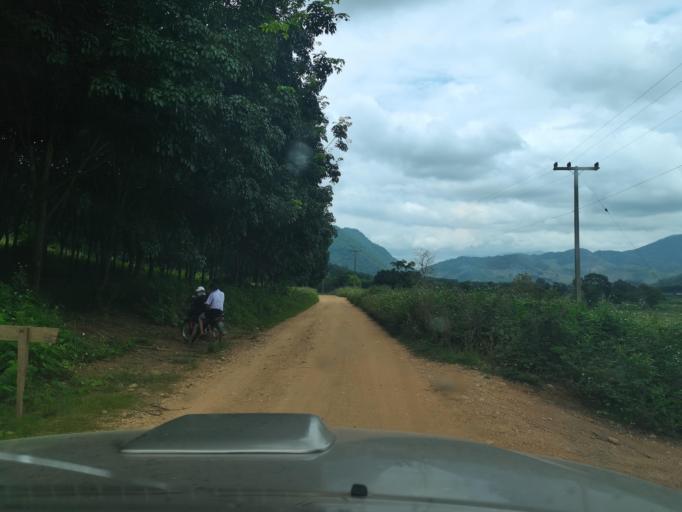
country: TH
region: Phayao
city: Phu Sang
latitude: 19.7415
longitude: 100.4486
